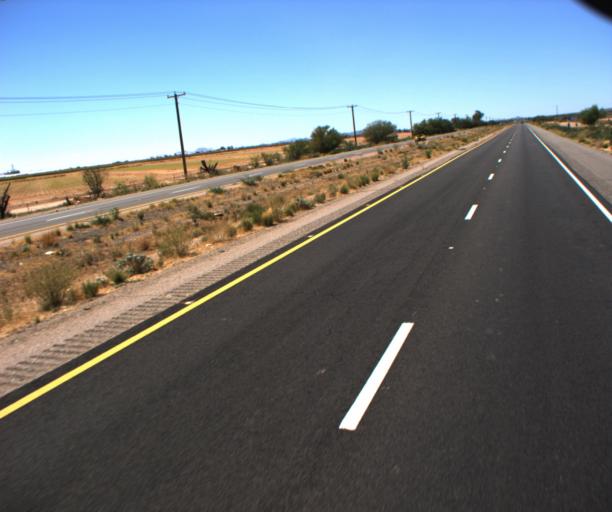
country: US
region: Arizona
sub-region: Pinal County
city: Maricopa
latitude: 32.9066
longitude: -112.0496
